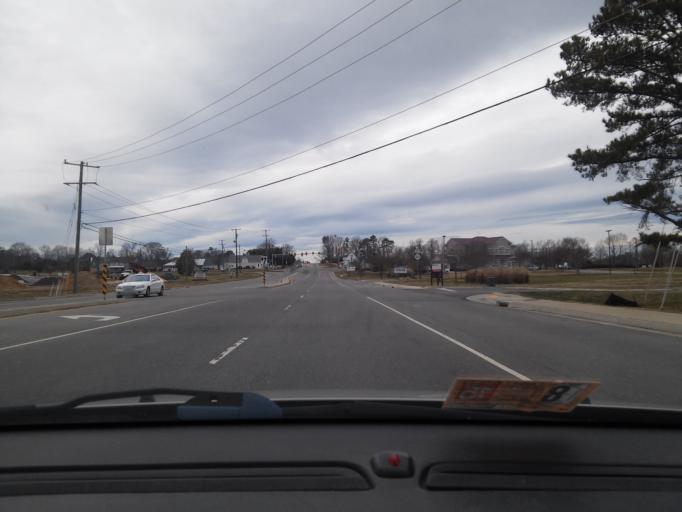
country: US
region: Virginia
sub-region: Henrico County
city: Short Pump
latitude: 37.6706
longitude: -77.6850
